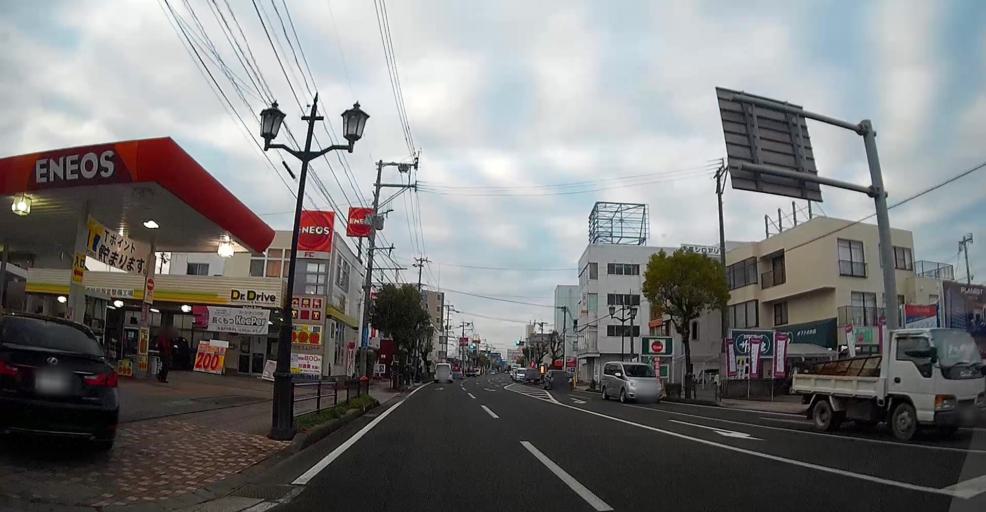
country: JP
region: Kumamoto
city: Hondo
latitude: 32.4515
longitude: 130.1969
